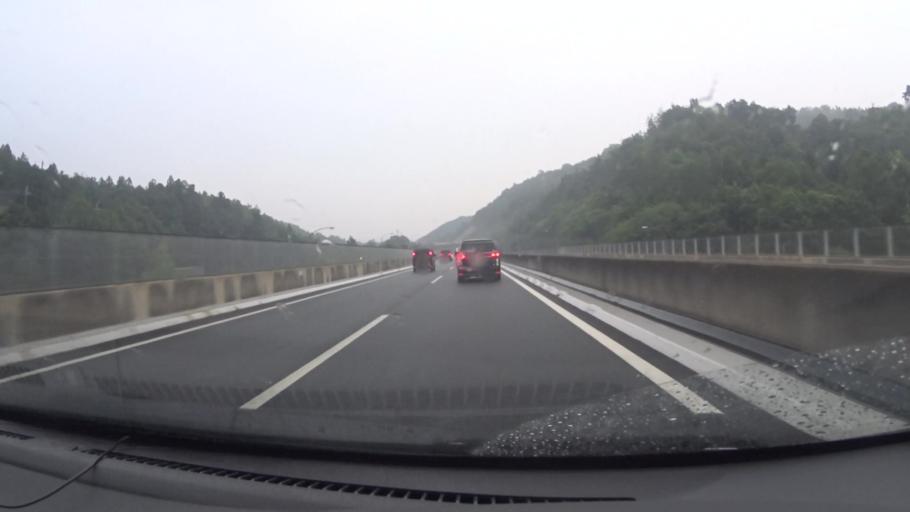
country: JP
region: Kyoto
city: Kameoka
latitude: 35.0083
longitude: 135.5617
